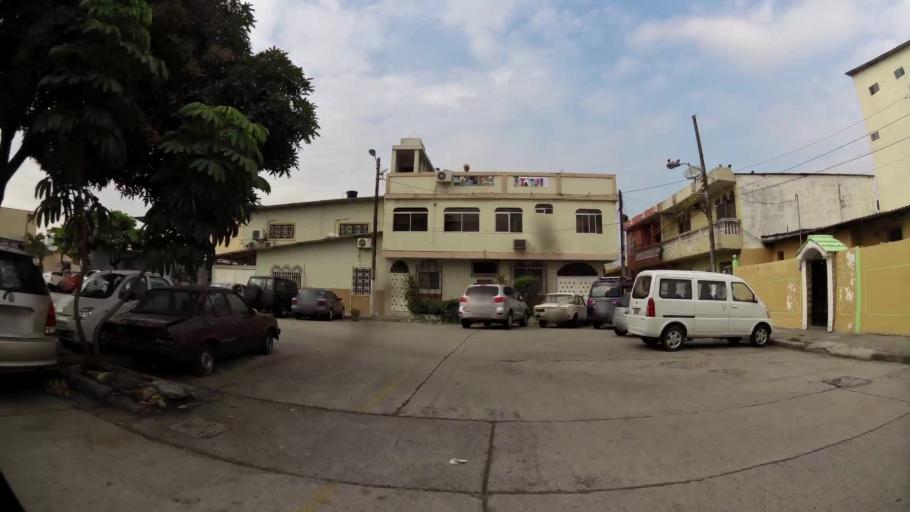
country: EC
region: Guayas
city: Eloy Alfaro
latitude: -2.1402
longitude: -79.8875
